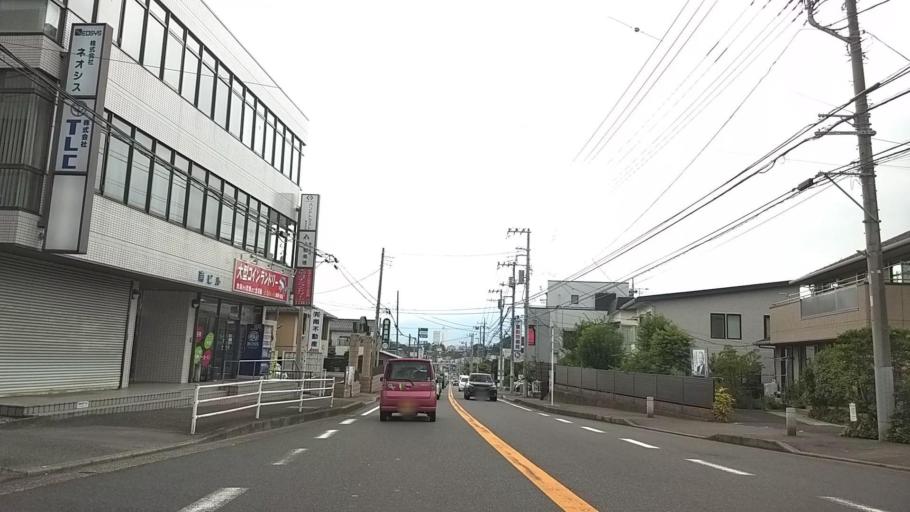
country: JP
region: Kanagawa
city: Zama
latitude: 35.4537
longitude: 139.4092
